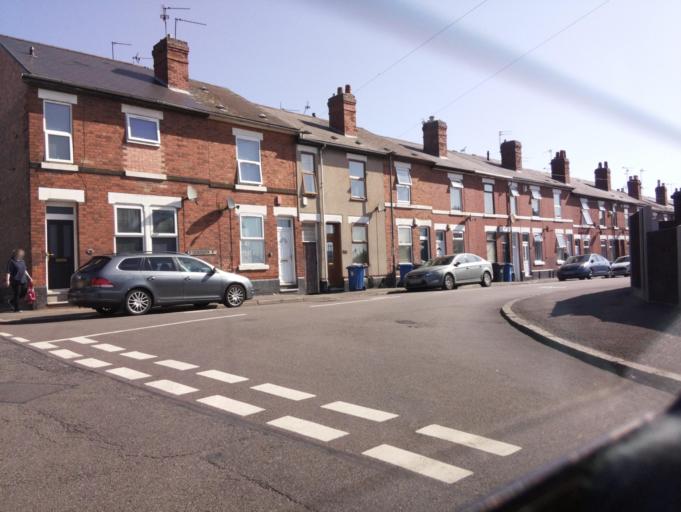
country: GB
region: England
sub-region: Derby
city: Derby
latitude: 52.9154
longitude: -1.4972
